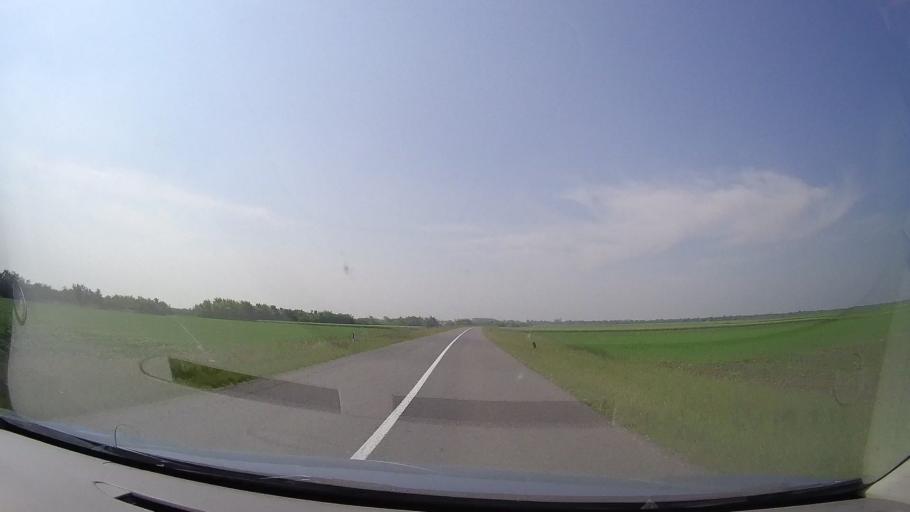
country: RS
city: Jarkovac
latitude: 45.2900
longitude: 20.7645
